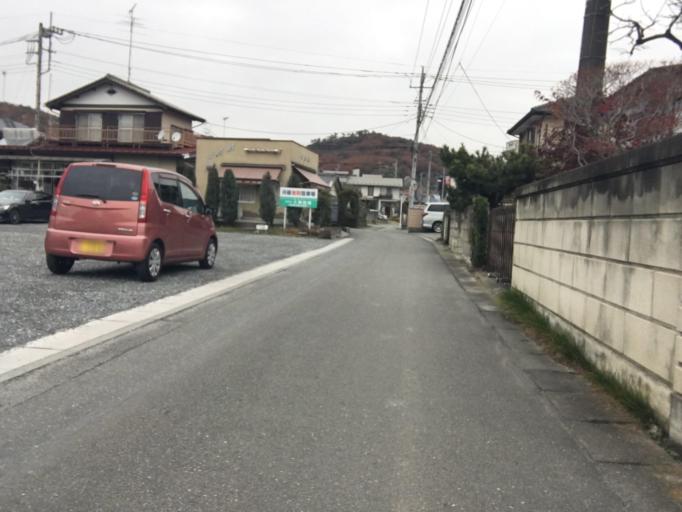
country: JP
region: Saitama
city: Yorii
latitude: 36.1205
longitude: 139.1930
